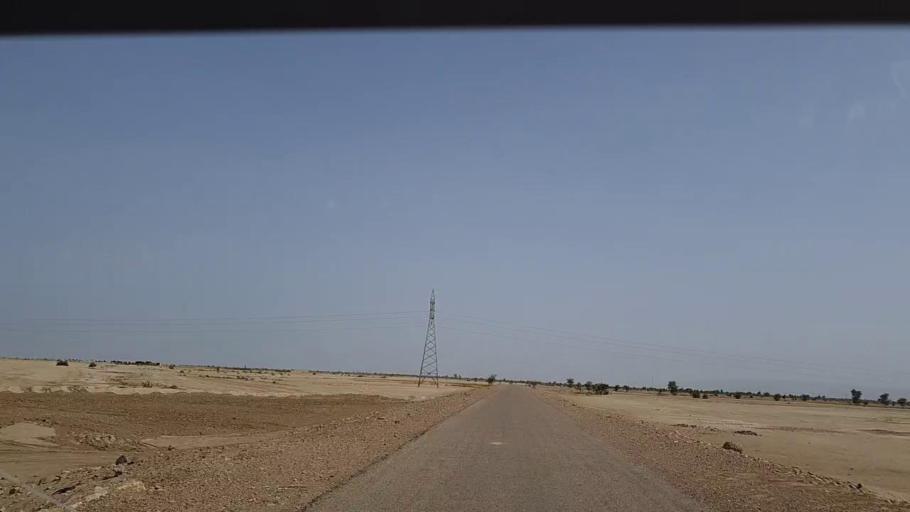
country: PK
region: Sindh
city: Johi
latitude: 26.6699
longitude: 67.5083
